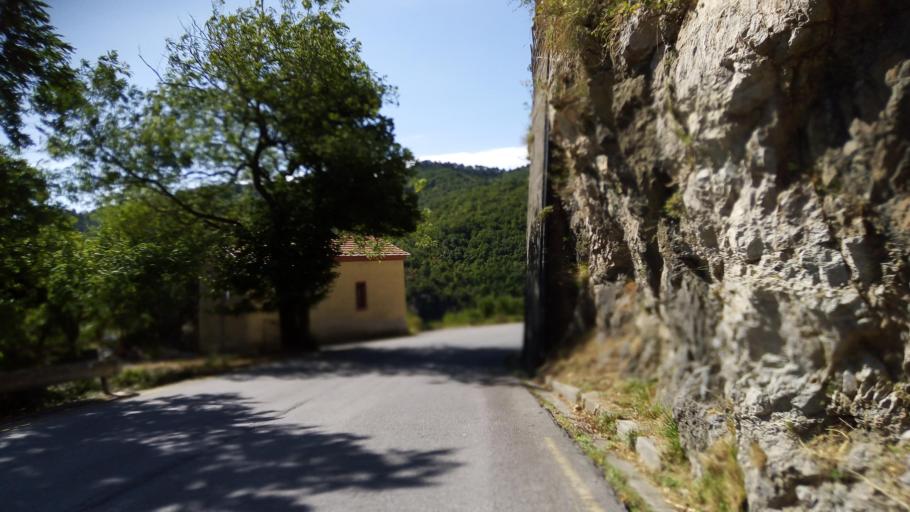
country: IT
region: Liguria
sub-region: Provincia di Savona
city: Balestrino
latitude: 44.1417
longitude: 8.1619
